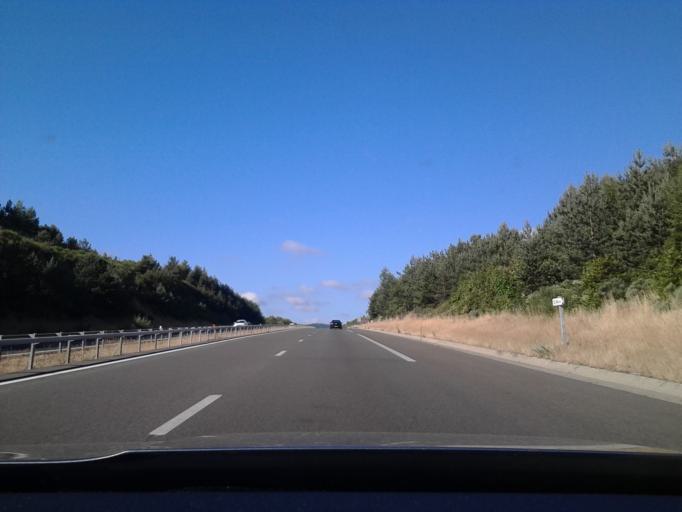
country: FR
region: Languedoc-Roussillon
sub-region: Departement de la Lozere
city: Aumont-Aubrac
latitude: 44.6535
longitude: 3.2514
